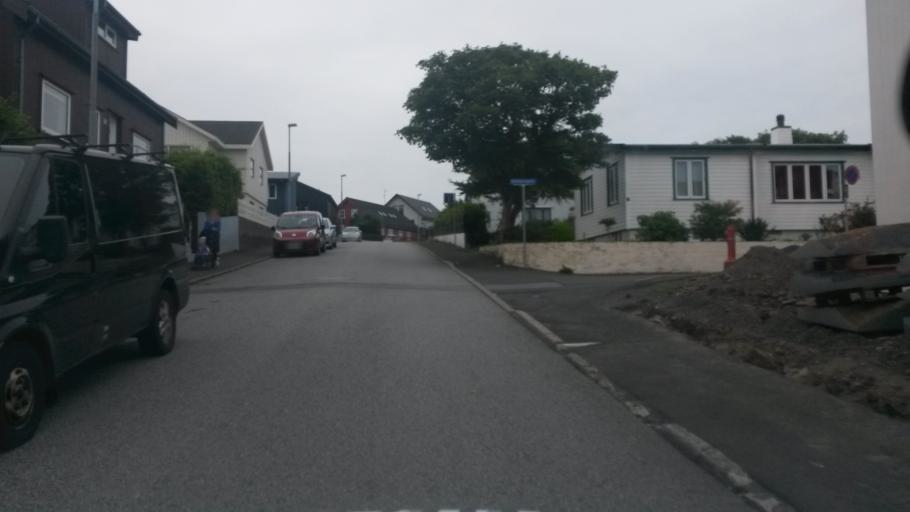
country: FO
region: Streymoy
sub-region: Torshavn
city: Torshavn
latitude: 62.0104
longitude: -6.7634
